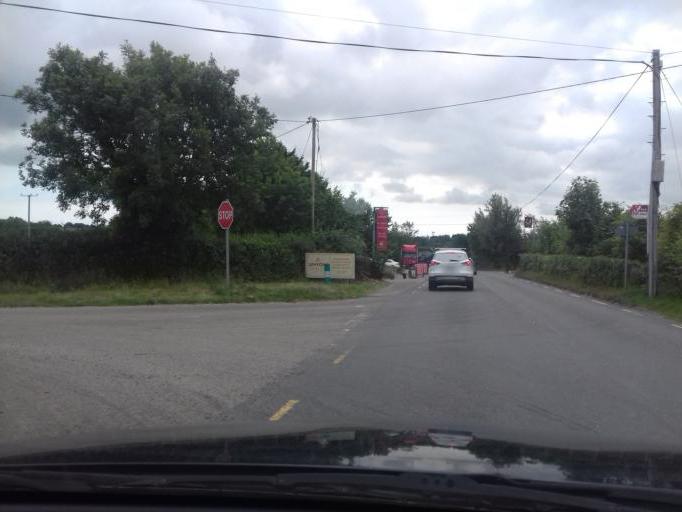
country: IE
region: Leinster
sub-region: Loch Garman
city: Ballinroad
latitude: 52.4532
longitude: -6.4008
